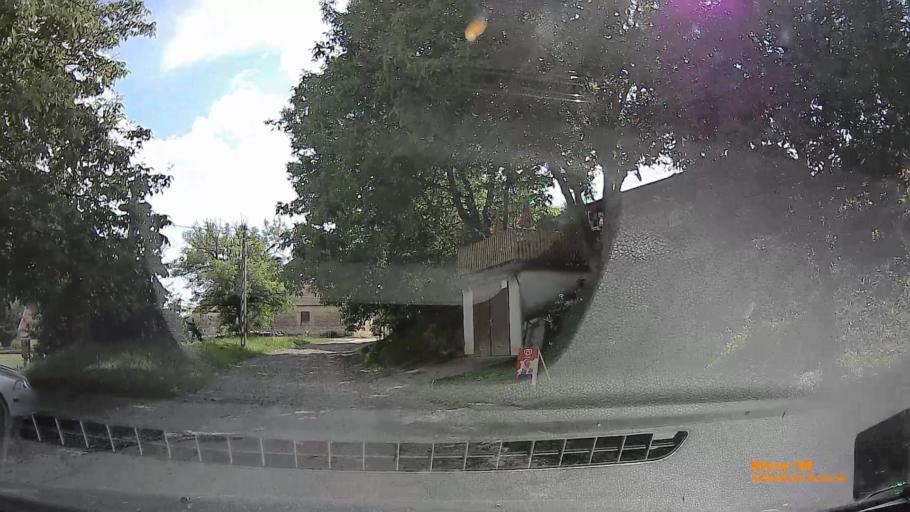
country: HU
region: Baranya
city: Kozarmisleny
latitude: 45.9841
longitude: 18.2631
